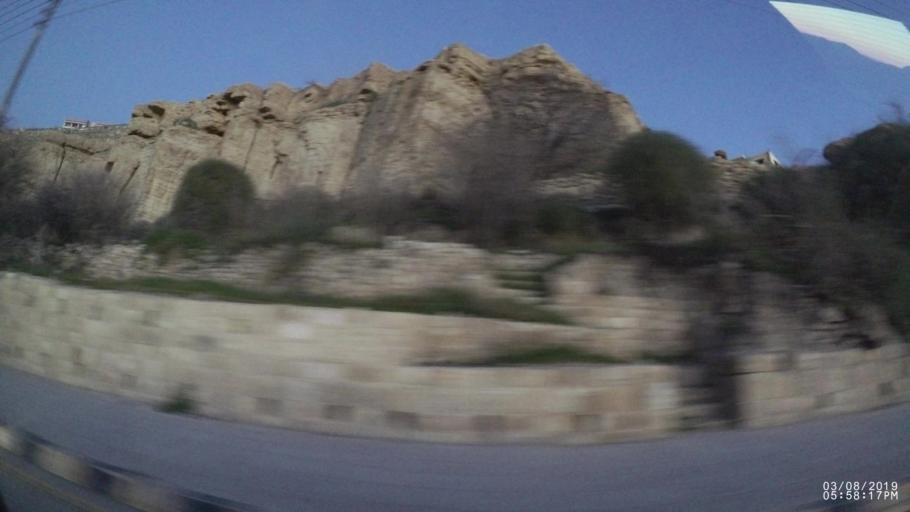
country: JO
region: Ma'an
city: Petra
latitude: 30.3255
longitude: 35.4749
